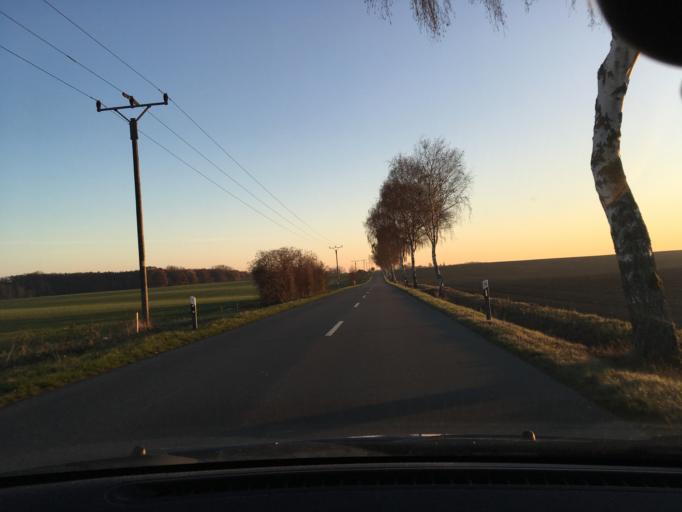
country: DE
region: Lower Saxony
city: Natendorf
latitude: 53.0938
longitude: 10.4674
